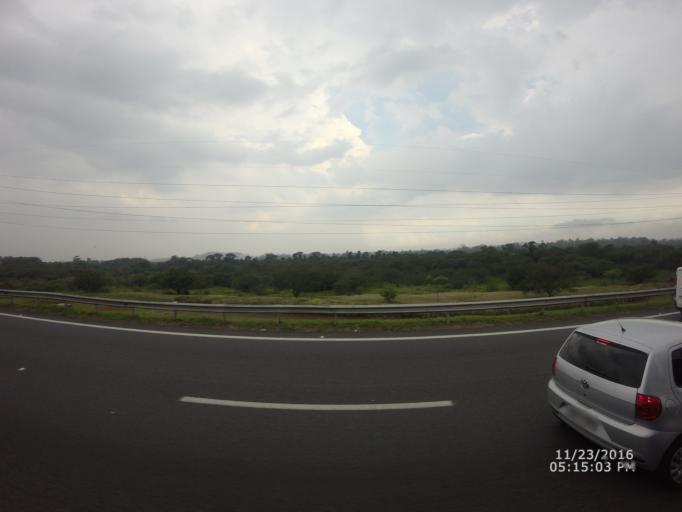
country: BR
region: Sao Paulo
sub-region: Guarulhos
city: Guarulhos
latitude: -23.4784
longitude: -46.5184
